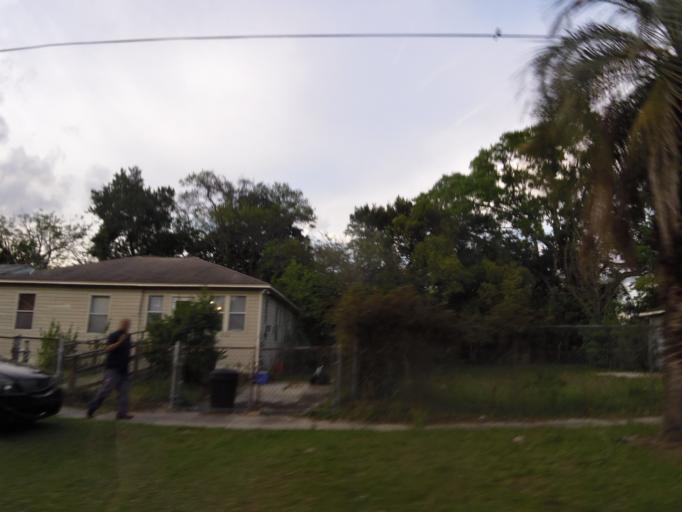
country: US
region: Florida
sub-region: Duval County
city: Jacksonville
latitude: 30.3605
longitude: -81.6287
